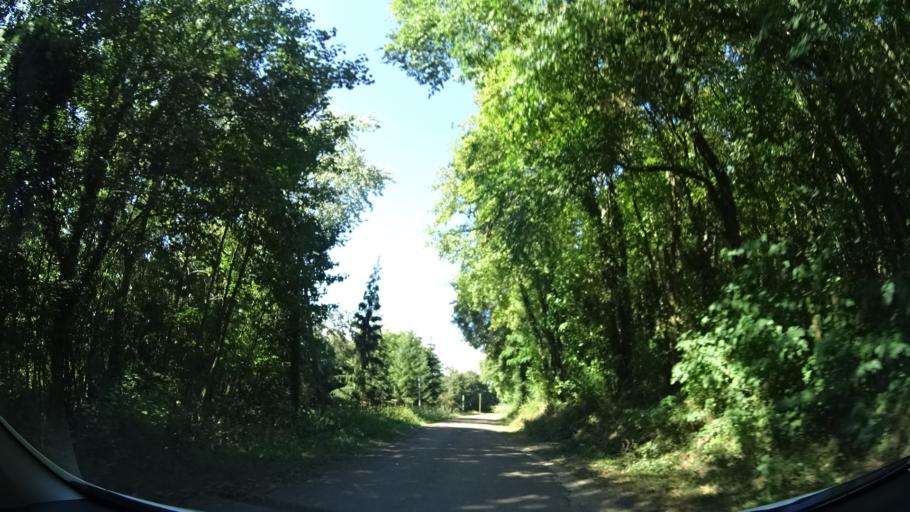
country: FR
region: Centre
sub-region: Departement du Loiret
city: Trigueres
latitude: 47.9468
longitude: 2.9851
